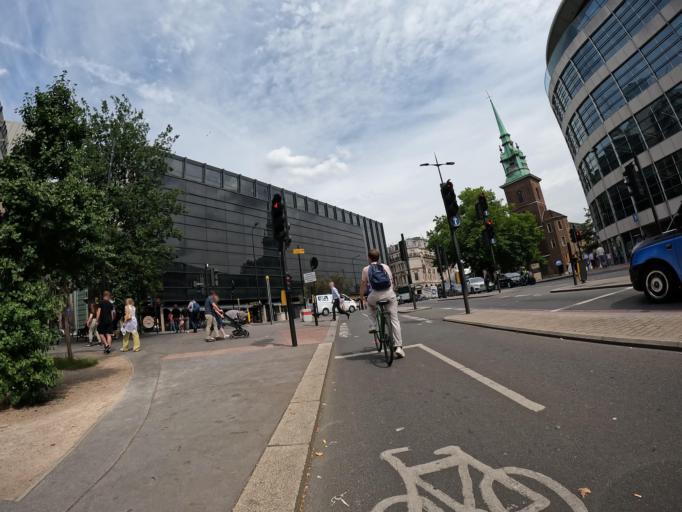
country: GB
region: England
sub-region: Greater London
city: Barbican
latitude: 51.5170
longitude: -0.1017
